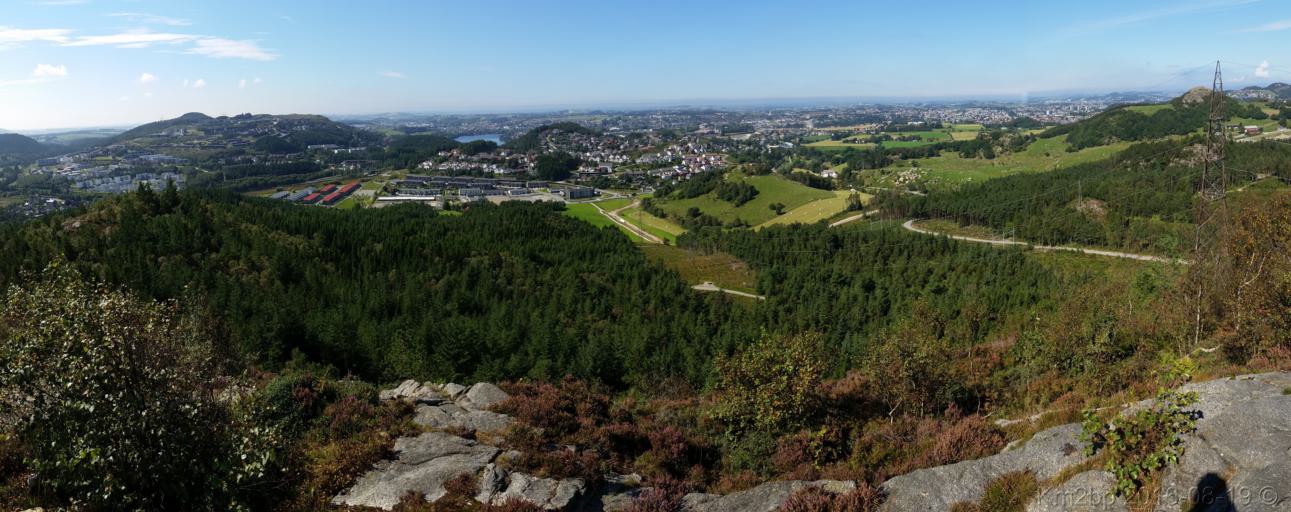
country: NO
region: Rogaland
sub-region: Sandnes
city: Sandnes
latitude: 58.8258
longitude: 5.7706
